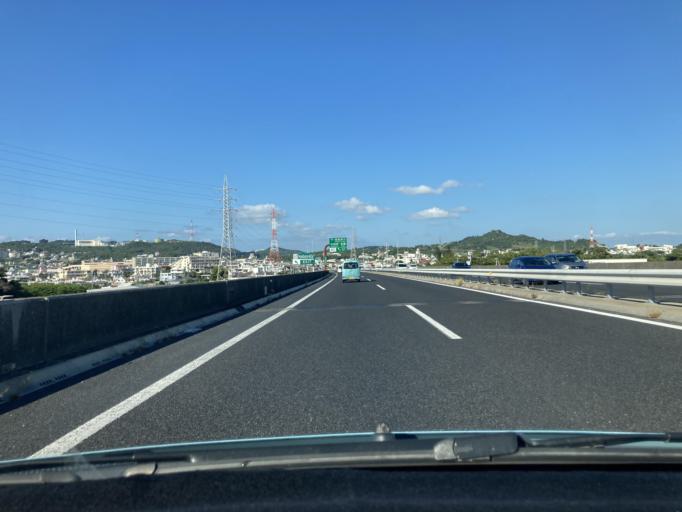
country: JP
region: Okinawa
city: Tomigusuku
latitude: 26.1922
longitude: 127.7391
